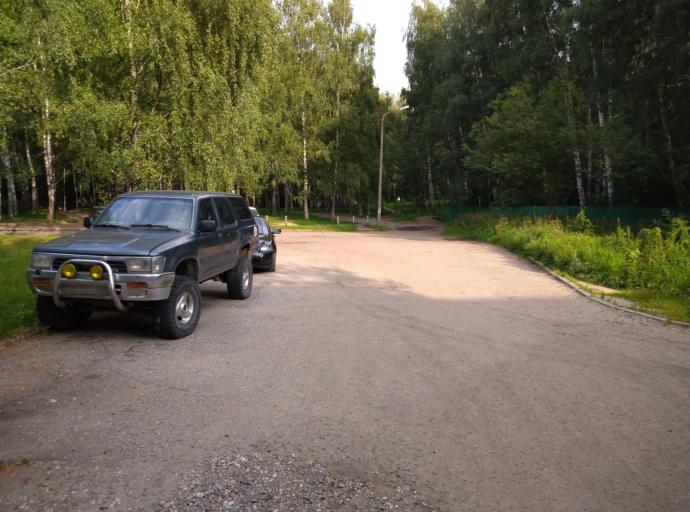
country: RU
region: Kostroma
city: Oktyabr'skiy
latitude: 57.7610
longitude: 40.9721
